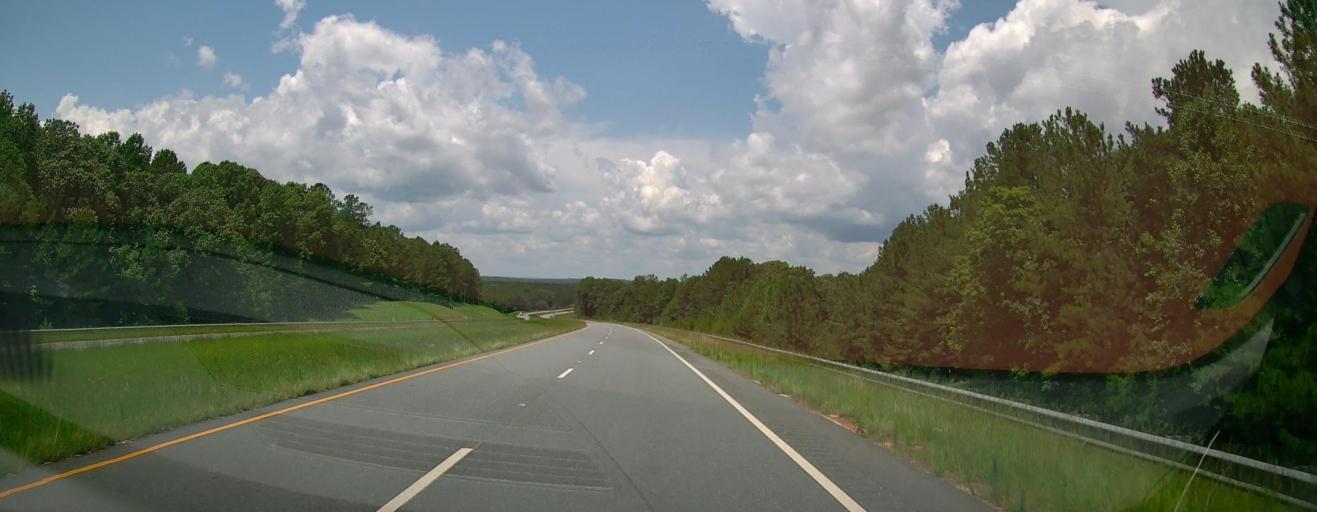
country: US
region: Georgia
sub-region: Upson County
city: Thomaston
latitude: 32.7919
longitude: -84.2554
